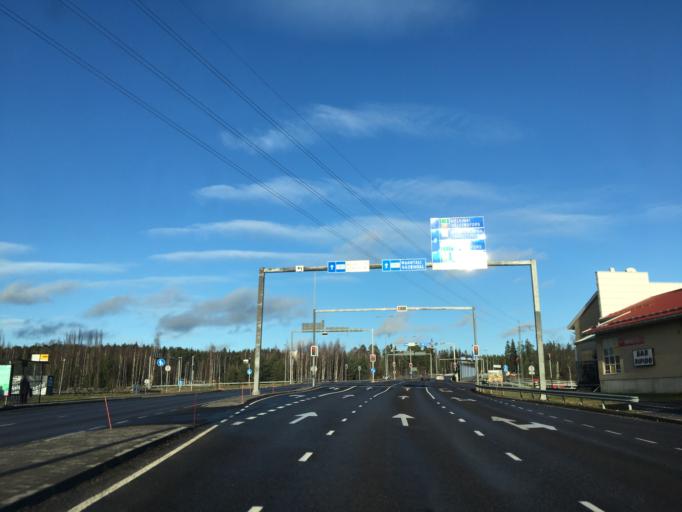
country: FI
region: Varsinais-Suomi
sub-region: Turku
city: Raisio
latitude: 60.4593
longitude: 22.1958
